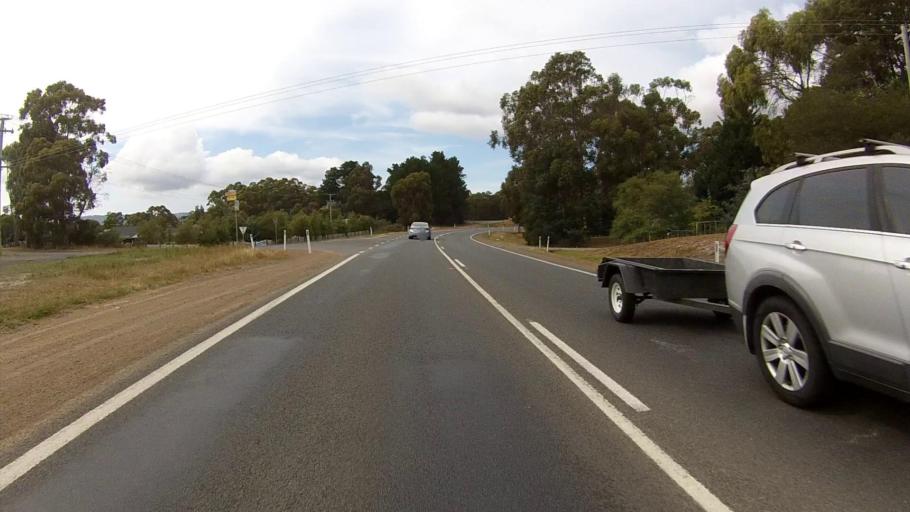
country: AU
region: Tasmania
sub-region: Kingborough
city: Margate
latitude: -43.0398
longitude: 147.2665
